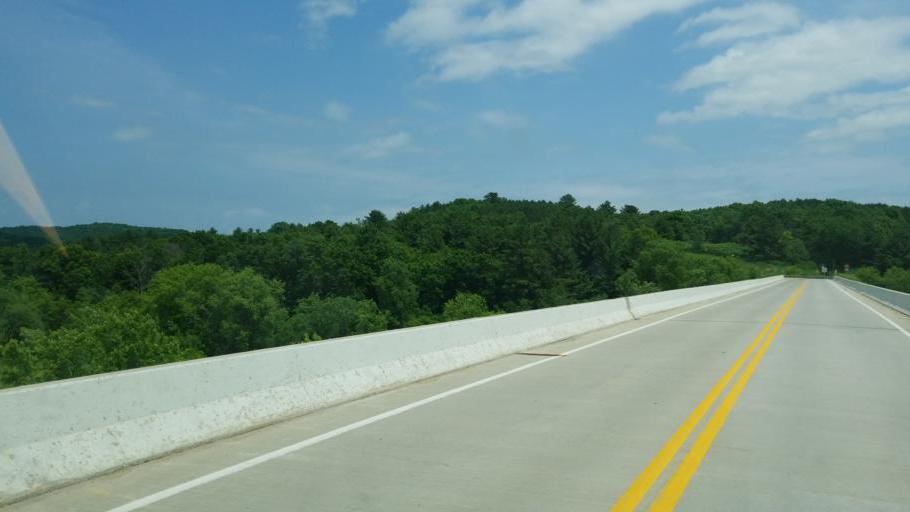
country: US
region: Wisconsin
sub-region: Monroe County
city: Cashton
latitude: 43.6396
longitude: -90.5992
